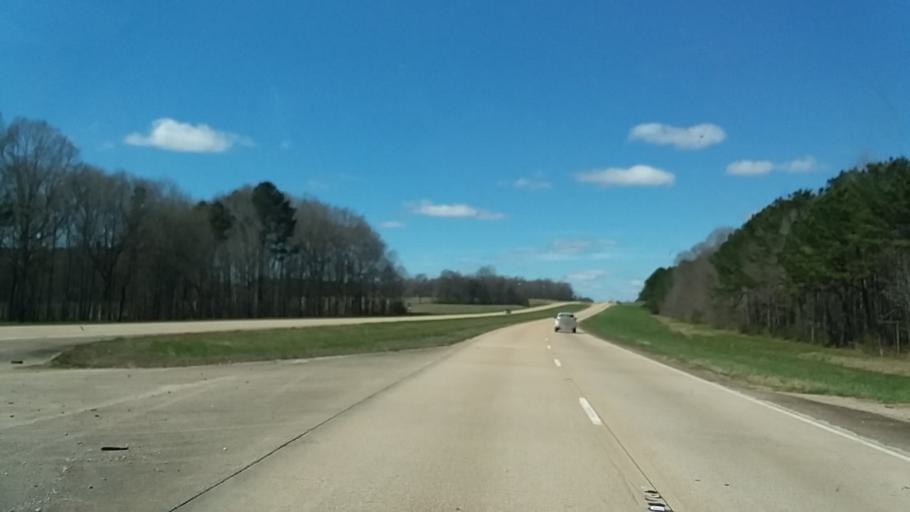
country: US
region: Mississippi
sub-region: Tishomingo County
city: Iuka
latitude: 34.8120
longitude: -88.2822
